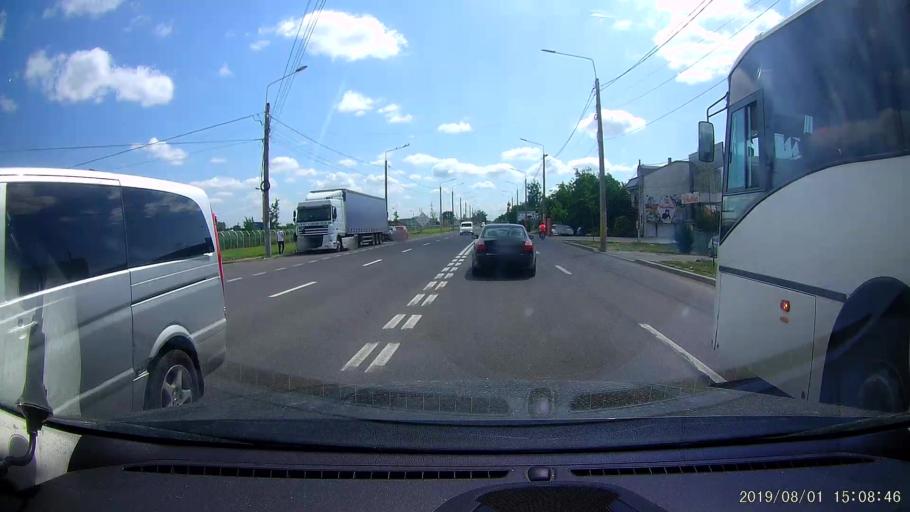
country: RO
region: Braila
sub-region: Municipiul Braila
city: Braila
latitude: 45.2390
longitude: 27.9432
